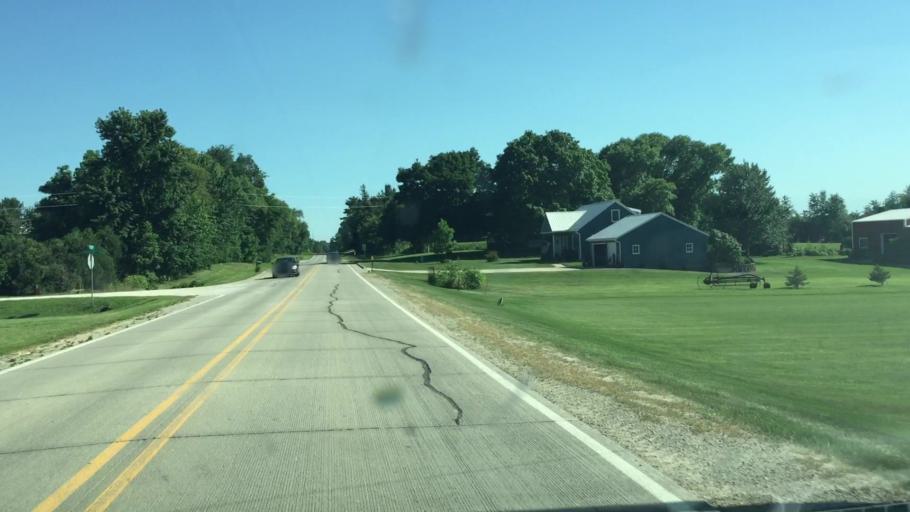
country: US
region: Iowa
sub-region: Linn County
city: Ely
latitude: 41.8626
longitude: -91.6464
